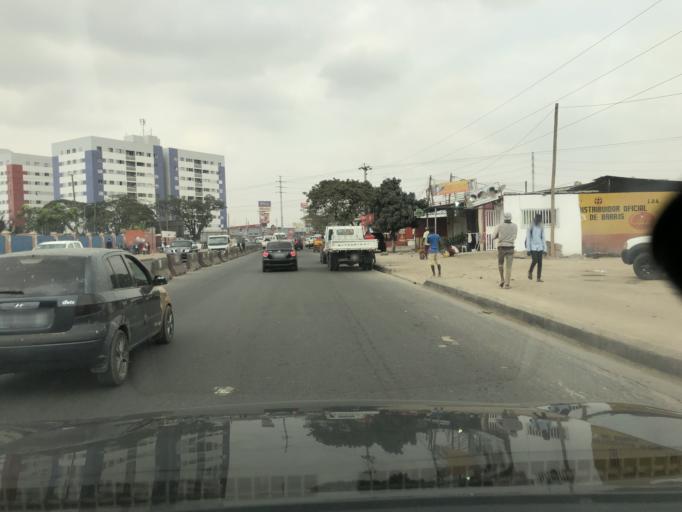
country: AO
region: Luanda
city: Luanda
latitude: -8.8464
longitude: 13.2846
